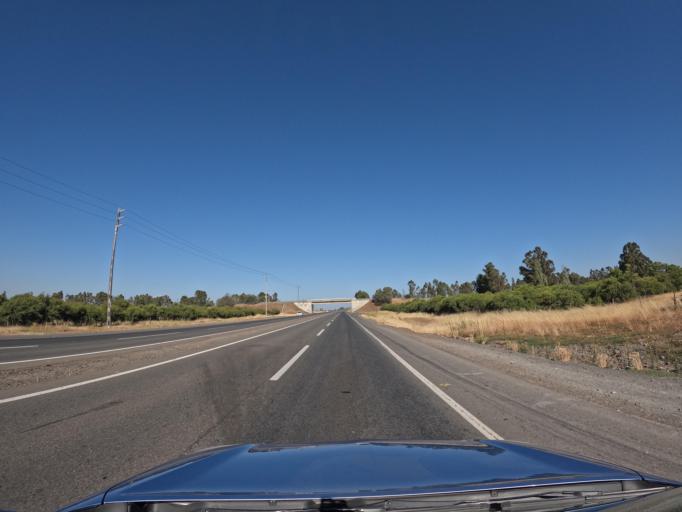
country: CL
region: Biobio
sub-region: Provincia de Nuble
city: Bulnes
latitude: -36.6588
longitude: -72.2794
